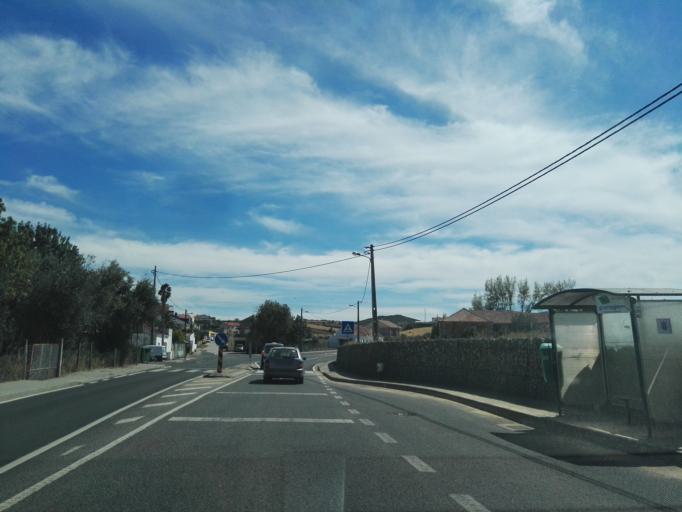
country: PT
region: Lisbon
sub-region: Arruda Dos Vinhos
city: Arruda dos Vinhos
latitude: 38.9597
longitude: -9.0592
